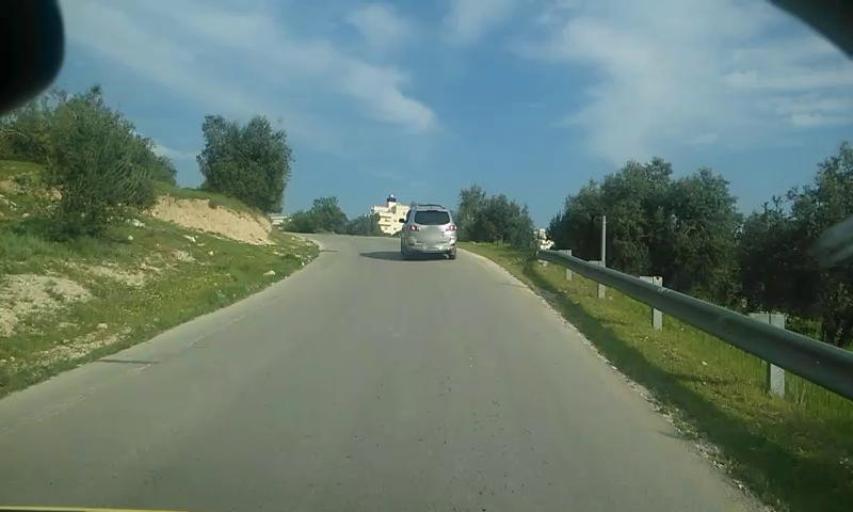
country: PS
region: West Bank
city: Nuba
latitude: 31.6144
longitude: 35.0219
